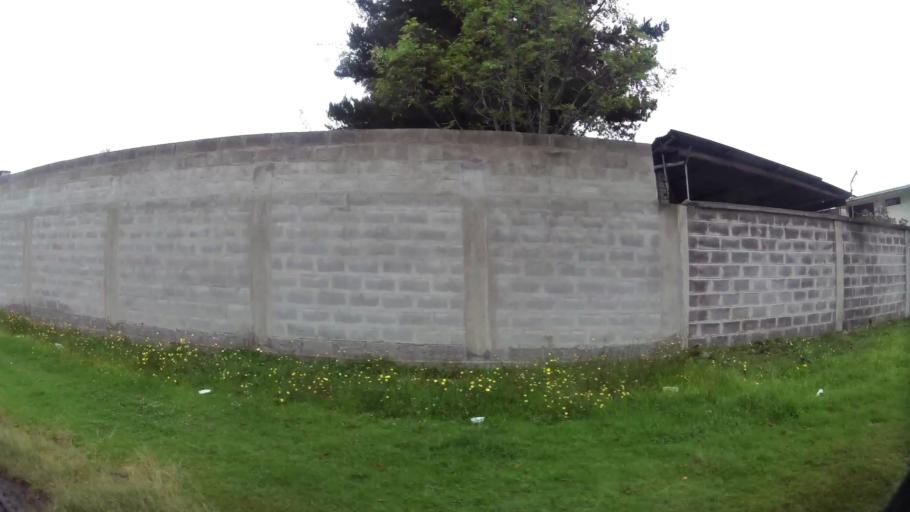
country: EC
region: Pichincha
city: Sangolqui
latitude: -0.2842
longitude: -78.4512
